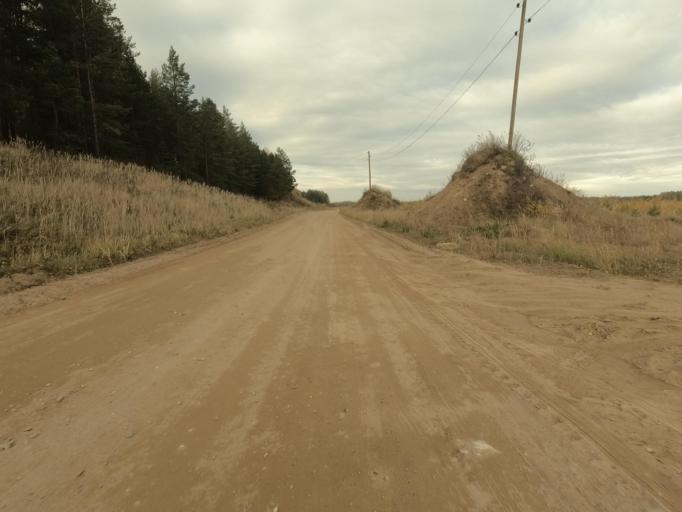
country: RU
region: Leningrad
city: Priladozhskiy
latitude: 59.6993
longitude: 31.3625
